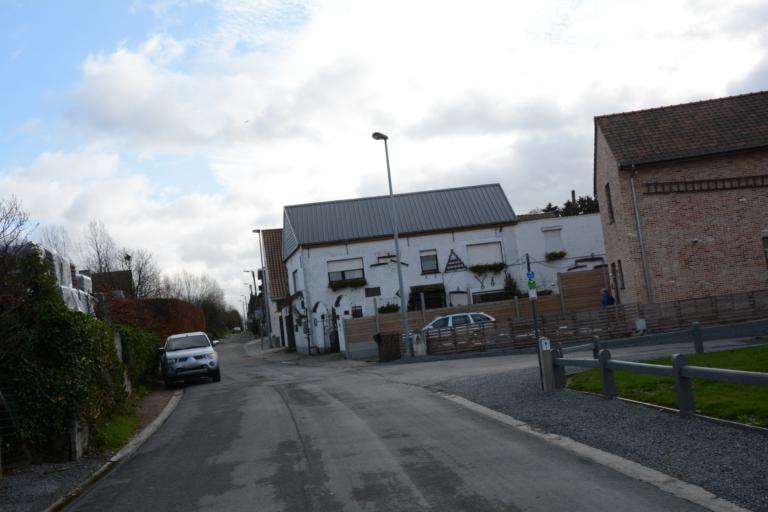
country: BE
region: Flanders
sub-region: Provincie Vlaams-Brabant
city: Opwijk
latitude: 50.9381
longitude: 4.1717
